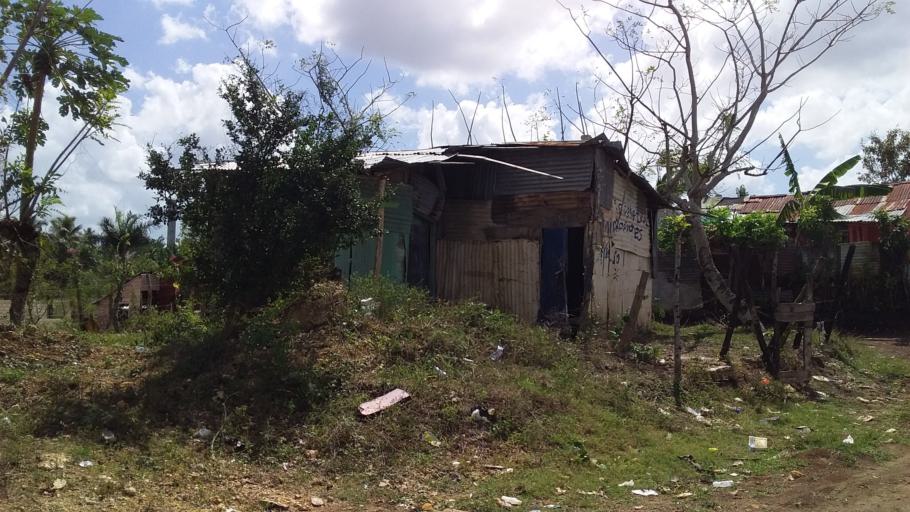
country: DO
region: Santo Domingo
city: Guerra
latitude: 18.5640
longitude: -69.7814
